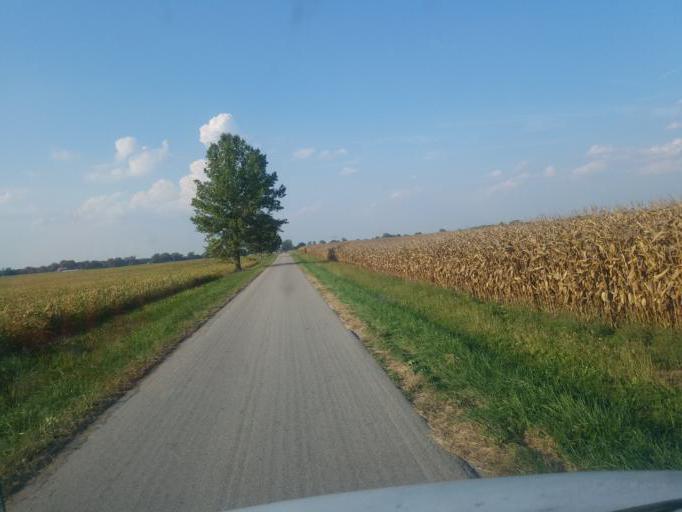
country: US
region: Ohio
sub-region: Wyandot County
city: Upper Sandusky
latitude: 40.9212
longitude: -83.1893
